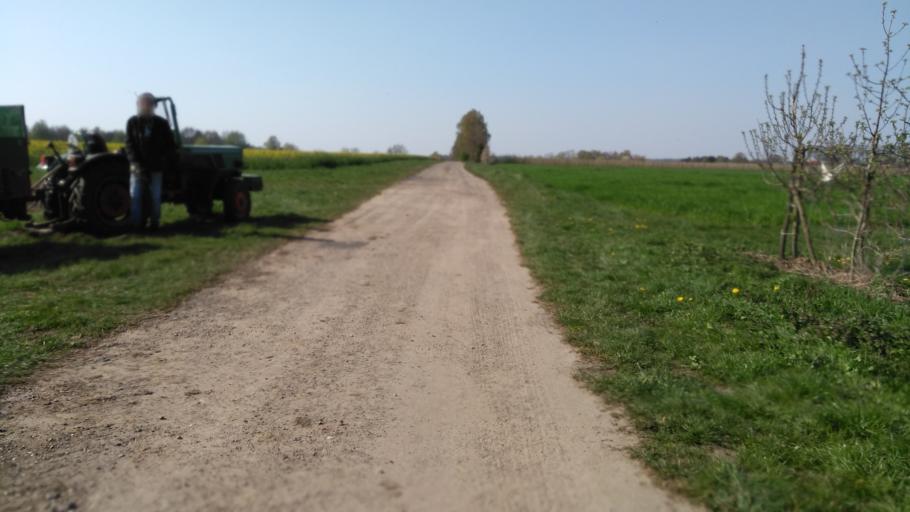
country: DE
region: Lower Saxony
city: Bliedersdorf
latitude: 53.4727
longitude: 9.5695
